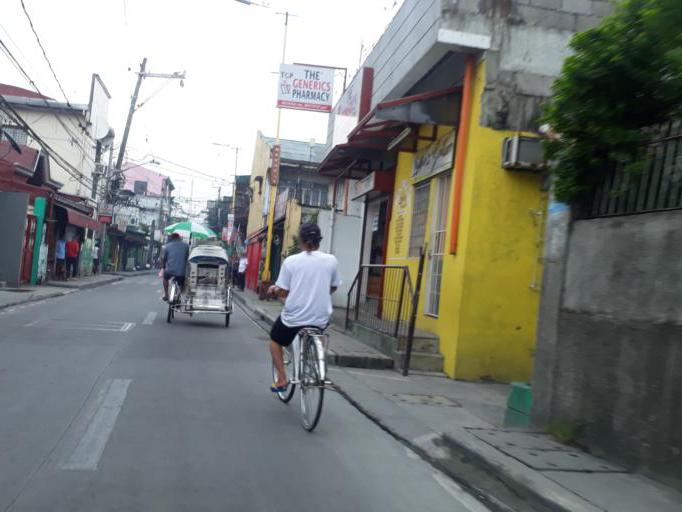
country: PH
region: Calabarzon
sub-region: Province of Rizal
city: Navotas
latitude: 14.6582
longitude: 120.9458
